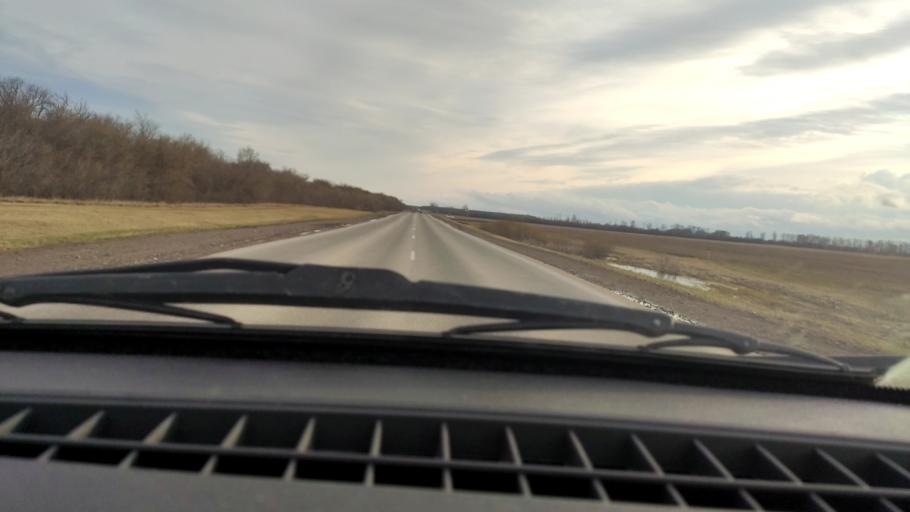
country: RU
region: Bashkortostan
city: Davlekanovo
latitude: 54.2772
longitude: 55.1052
